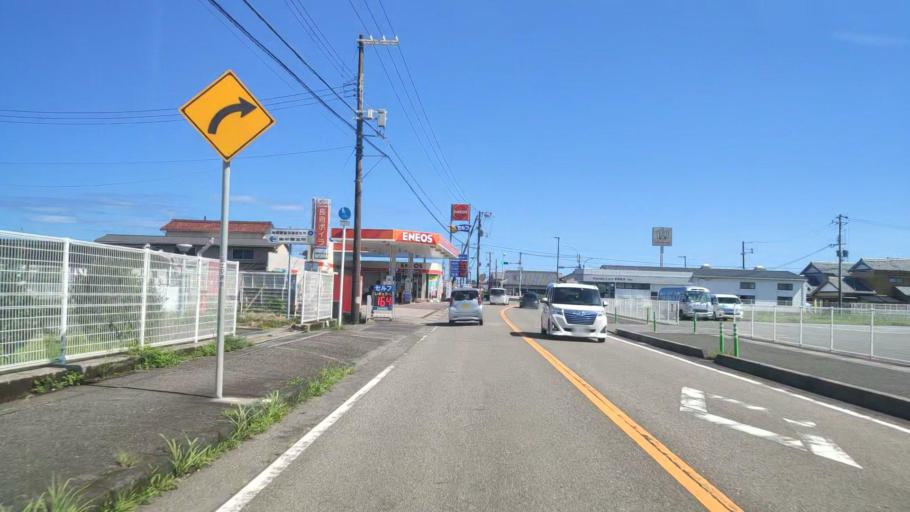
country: JP
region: Wakayama
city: Shingu
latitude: 33.5830
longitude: 135.9200
